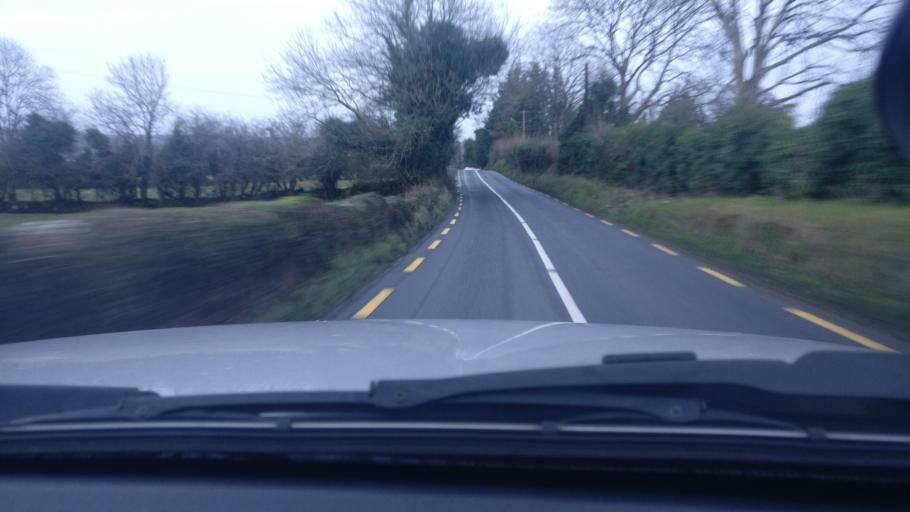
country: IE
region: Connaught
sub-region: County Galway
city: Loughrea
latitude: 53.1612
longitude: -8.5116
